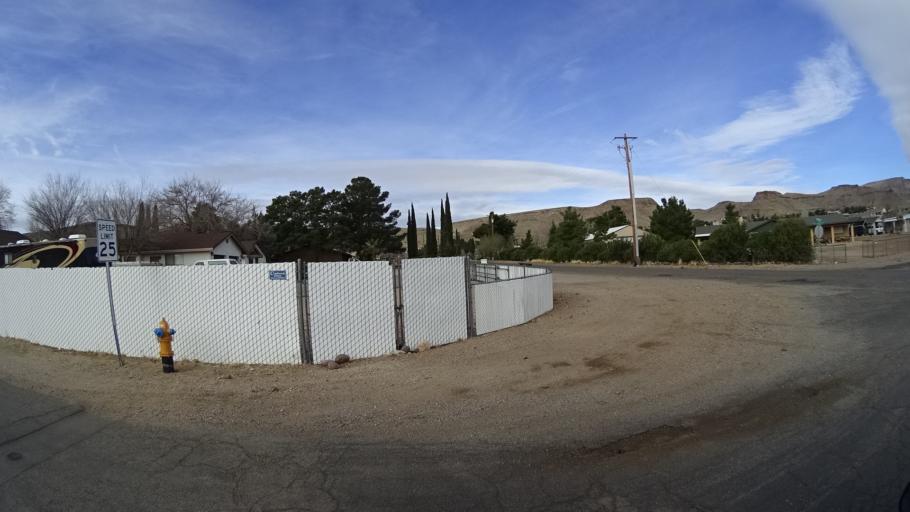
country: US
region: Arizona
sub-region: Mohave County
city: New Kingman-Butler
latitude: 35.2304
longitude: -114.0492
